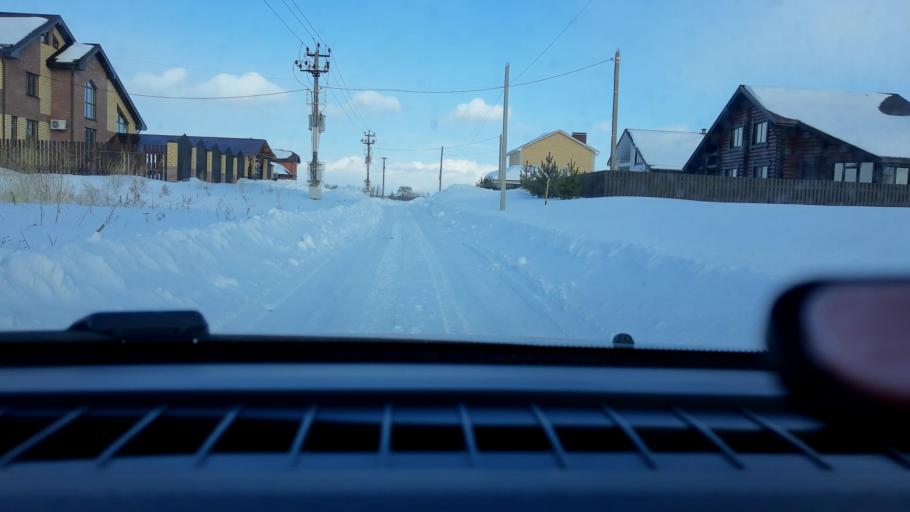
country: RU
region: Nizjnij Novgorod
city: Lukino
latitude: 56.4219
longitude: 43.7243
